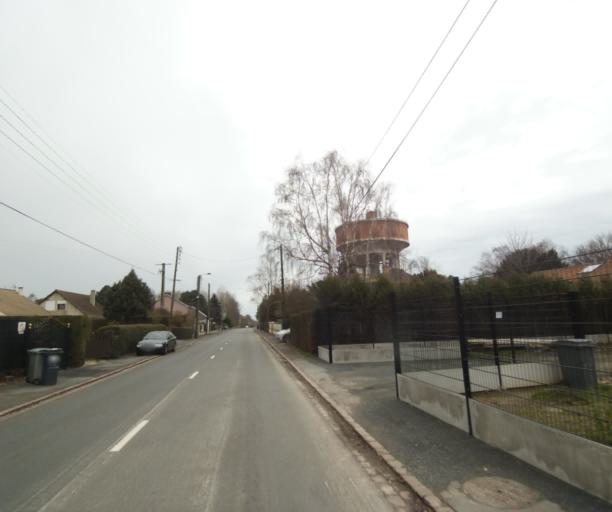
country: FR
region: Nord-Pas-de-Calais
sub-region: Departement du Nord
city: Quievrechain
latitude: 50.3810
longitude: 3.6579
